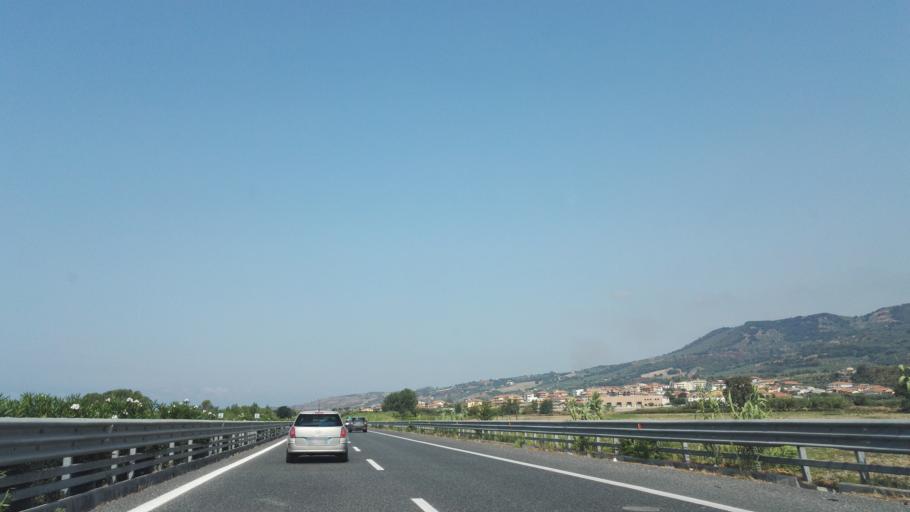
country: IT
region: Calabria
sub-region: Provincia di Catanzaro
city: Santa Eufemia Lamezia
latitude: 38.9347
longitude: 16.2189
